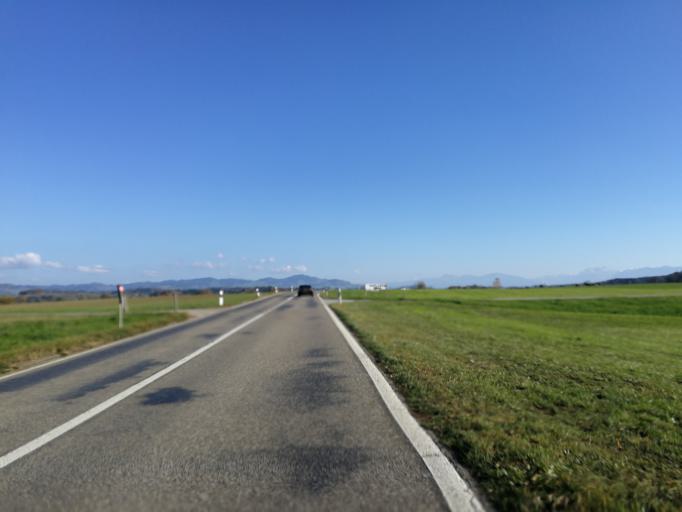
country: CH
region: Zurich
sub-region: Bezirk Uster
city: Egg
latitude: 47.3149
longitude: 8.7018
